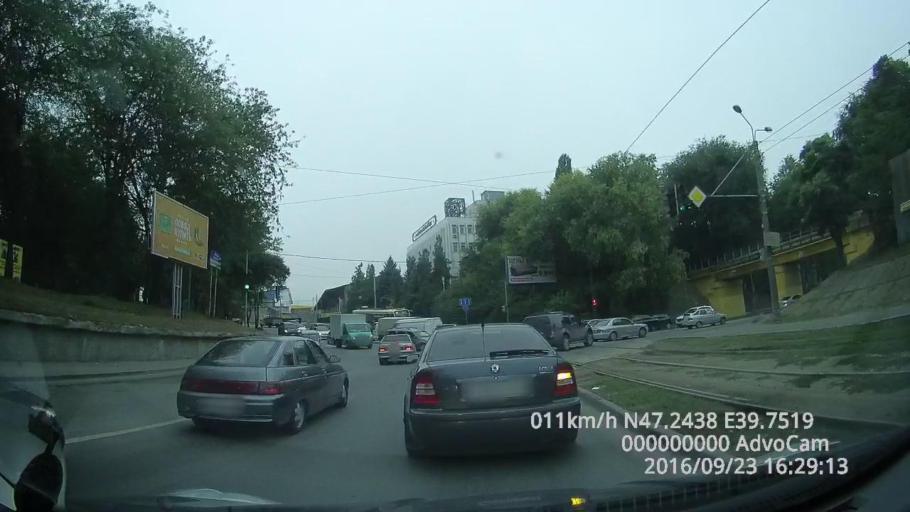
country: RU
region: Rostov
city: Rostov-na-Donu
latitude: 47.2437
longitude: 39.7519
